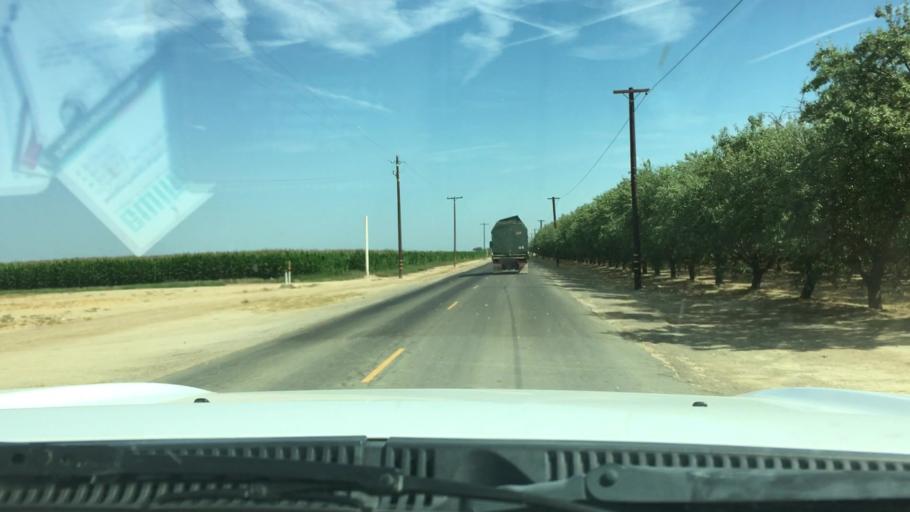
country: US
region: California
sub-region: Kern County
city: Shafter
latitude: 35.4784
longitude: -119.3680
